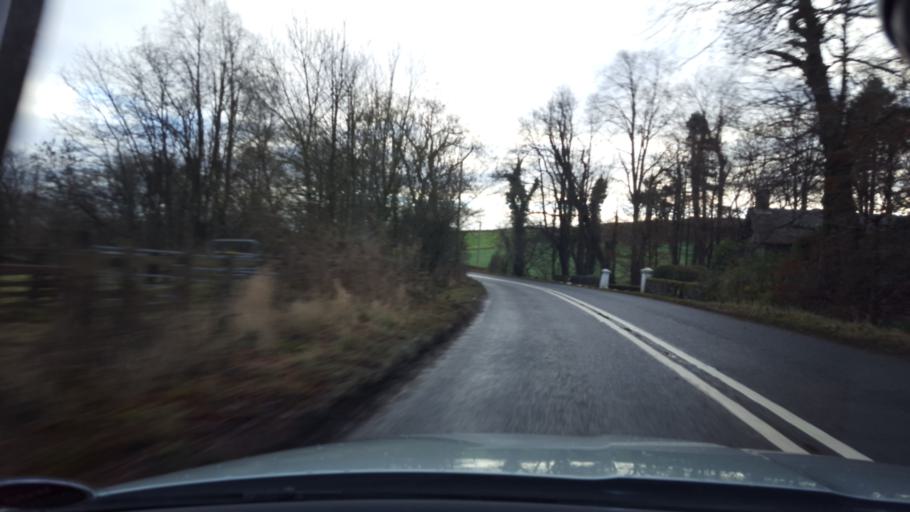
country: GB
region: Scotland
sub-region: Perth and Kinross
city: Milnathort
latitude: 56.2660
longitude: -3.3847
